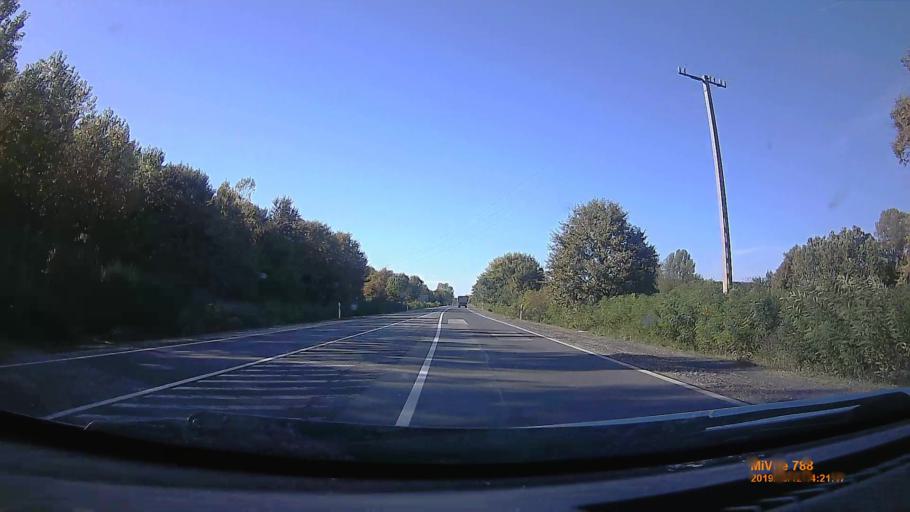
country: HU
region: Hajdu-Bihar
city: Biharkeresztes
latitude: 47.1404
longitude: 21.7272
